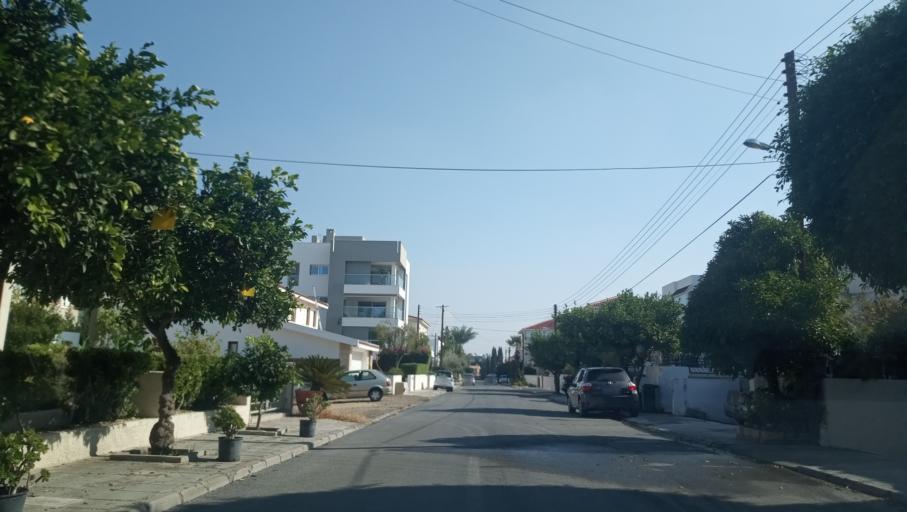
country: CY
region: Lefkosia
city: Nicosia
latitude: 35.1454
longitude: 33.3858
